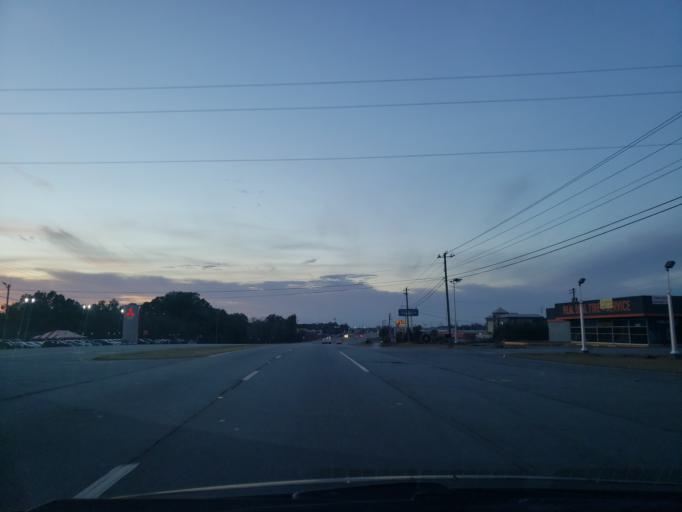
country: US
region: Georgia
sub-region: Dougherty County
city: Albany
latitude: 31.5727
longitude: -84.1269
